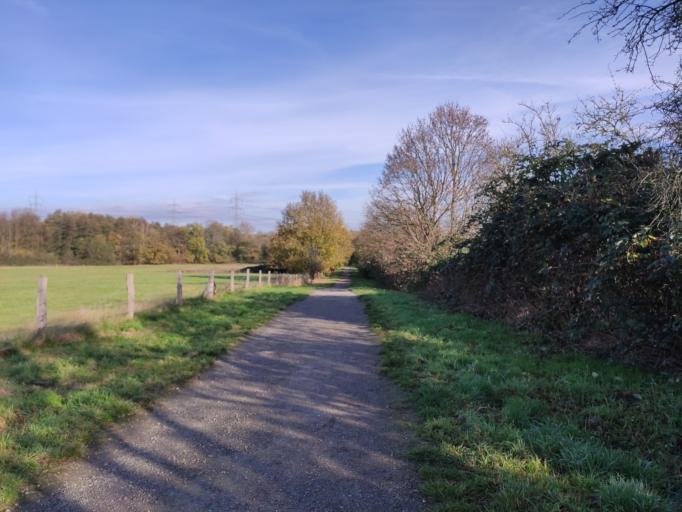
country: DE
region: North Rhine-Westphalia
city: Herten
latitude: 51.5890
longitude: 7.1074
